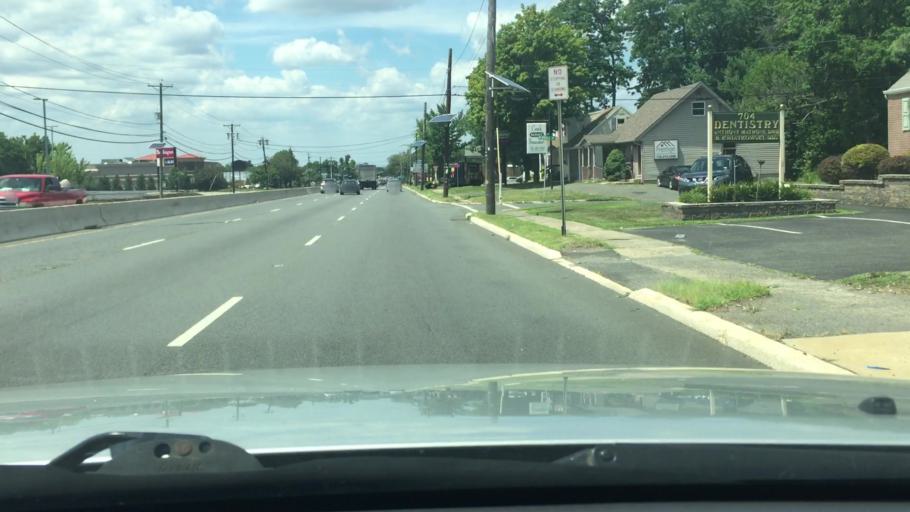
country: US
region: New Jersey
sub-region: Middlesex County
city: South River
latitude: 40.4294
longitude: -74.3841
